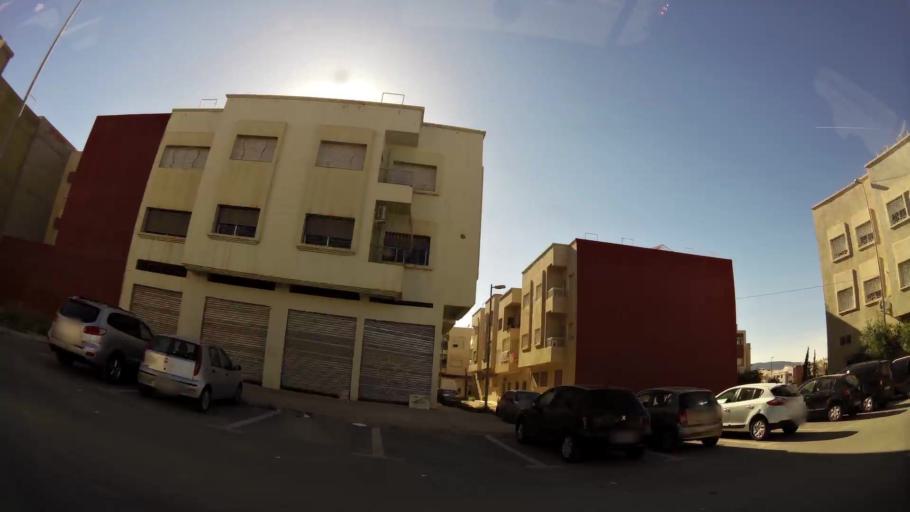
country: MA
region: Fes-Boulemane
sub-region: Fes
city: Fes
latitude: 34.0084
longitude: -5.0164
